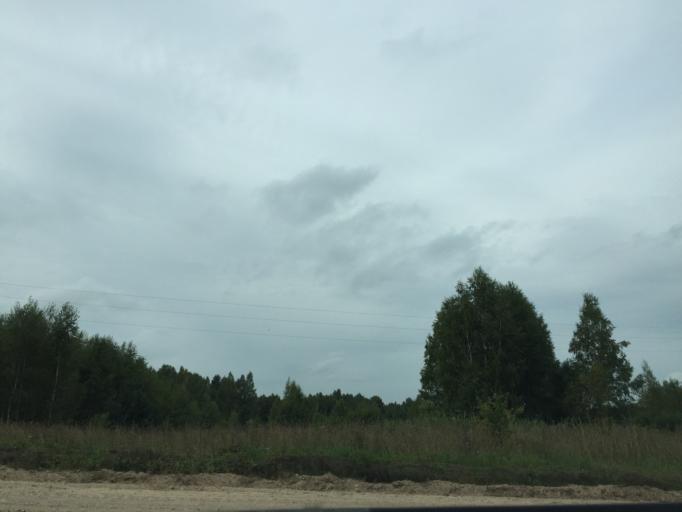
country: LV
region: Dagda
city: Dagda
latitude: 56.2447
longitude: 27.7930
